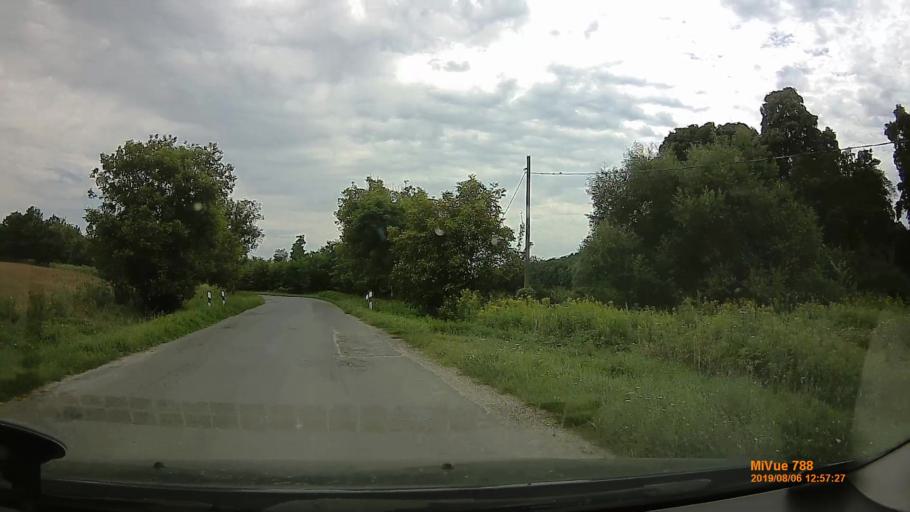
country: HU
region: Zala
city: Pacsa
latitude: 46.6314
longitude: 17.0396
